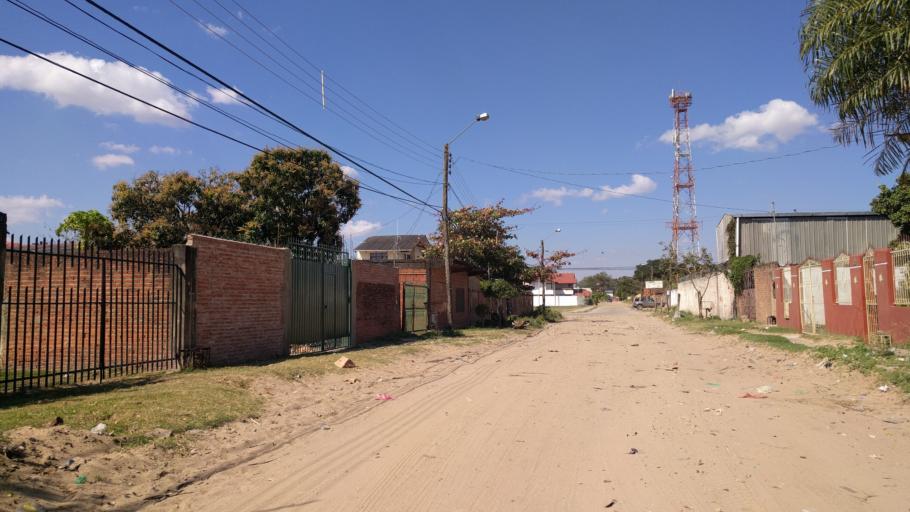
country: BO
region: Santa Cruz
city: Santa Cruz de la Sierra
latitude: -17.7989
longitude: -63.2168
